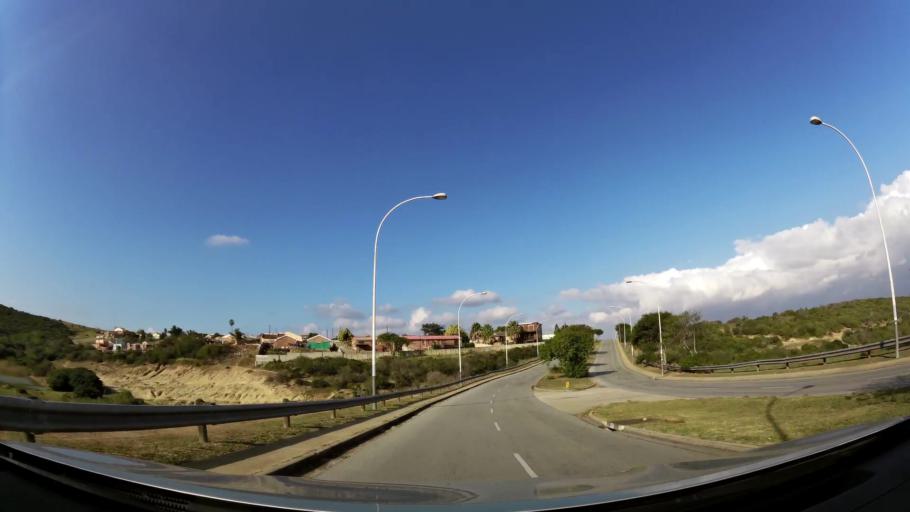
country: ZA
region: Eastern Cape
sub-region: Nelson Mandela Bay Metropolitan Municipality
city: Uitenhage
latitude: -33.7703
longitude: 25.4251
